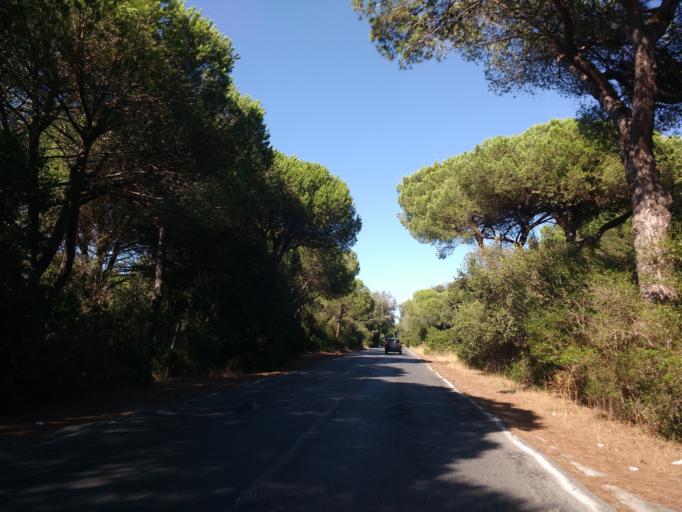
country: IT
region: Latium
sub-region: Citta metropolitana di Roma Capitale
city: Acilia-Castel Fusano-Ostia Antica
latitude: 41.7061
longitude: 12.3526
